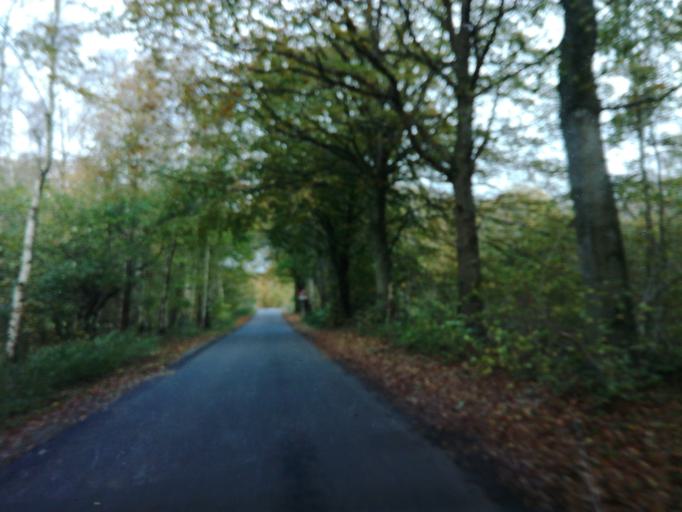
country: DK
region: South Denmark
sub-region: Vejle Kommune
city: Borkop
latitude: 55.6788
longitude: 9.6019
